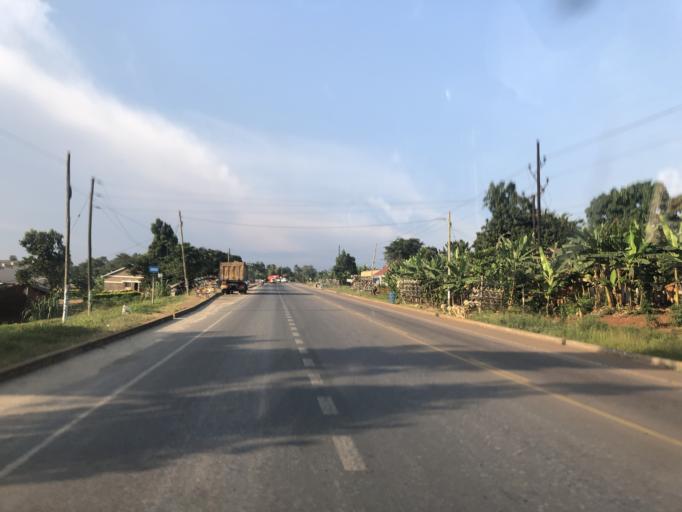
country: UG
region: Central Region
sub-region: Mpigi District
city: Mpigi
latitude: 0.1695
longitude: 32.2598
